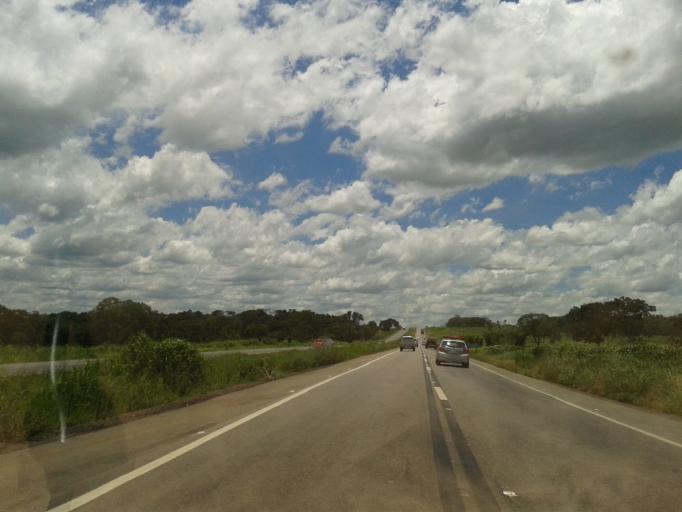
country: BR
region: Goias
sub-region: Jaragua
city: Jaragua
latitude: -15.9099
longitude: -49.2490
